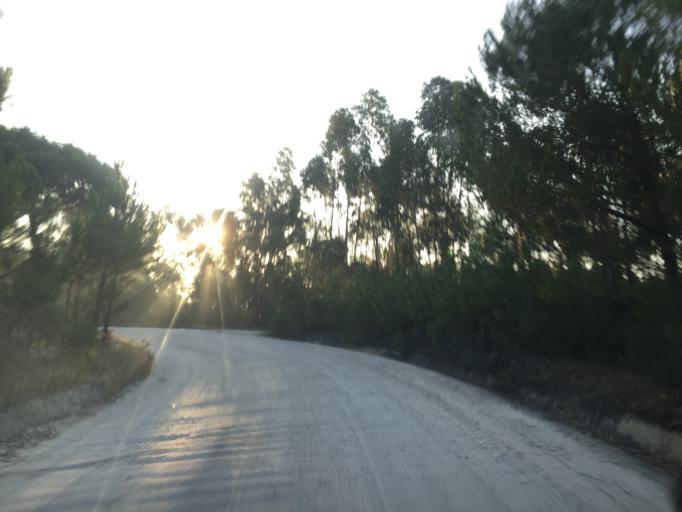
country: PT
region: Portalegre
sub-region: Ponte de Sor
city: Santo Andre
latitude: 39.0672
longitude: -8.4029
